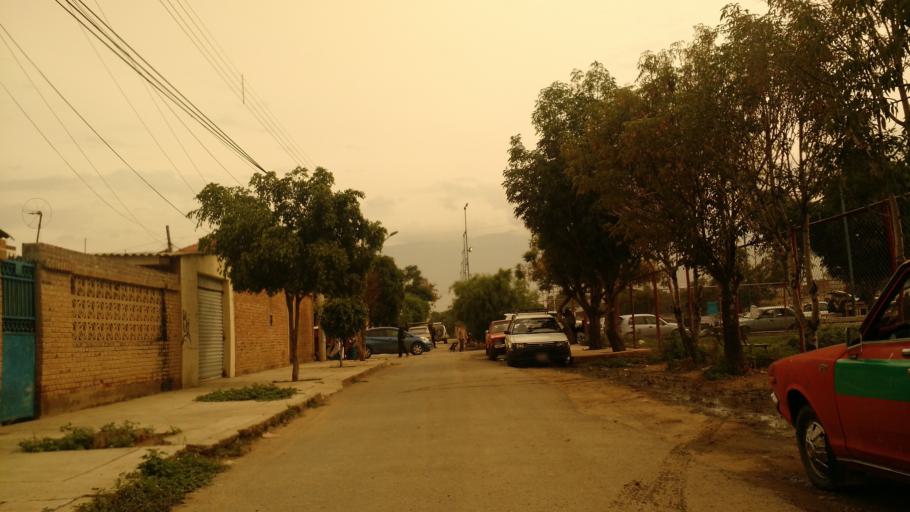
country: BO
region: Cochabamba
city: Cochabamba
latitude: -17.4273
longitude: -66.1564
